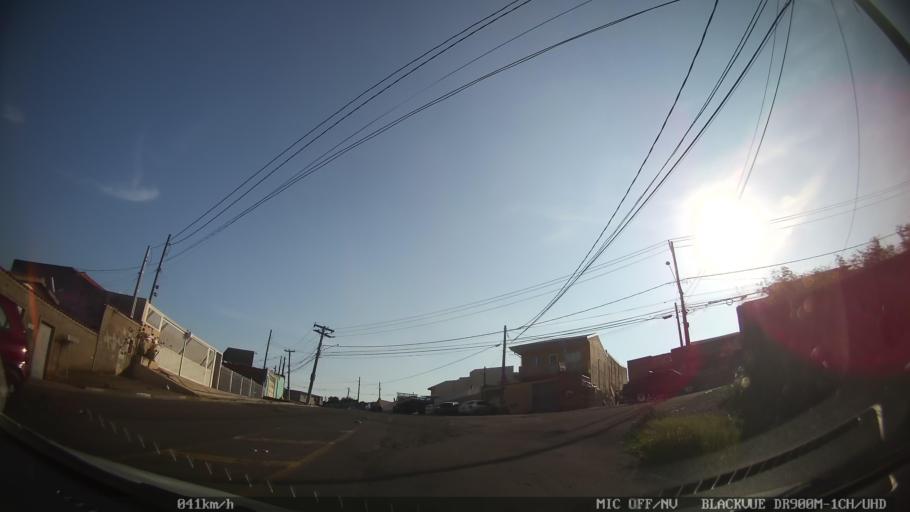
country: BR
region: Sao Paulo
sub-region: Campinas
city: Campinas
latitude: -22.9826
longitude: -47.1469
